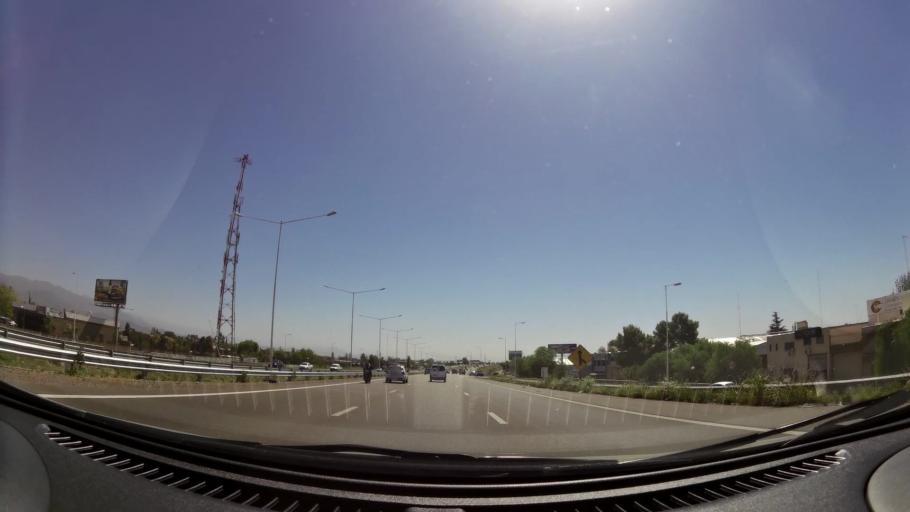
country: AR
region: Mendoza
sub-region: Departamento de Godoy Cruz
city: Godoy Cruz
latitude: -32.9388
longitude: -68.8300
